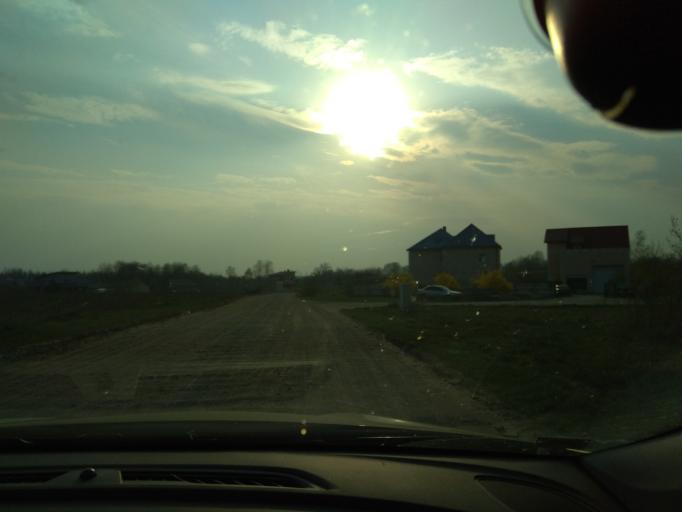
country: LT
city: Baltoji Voke
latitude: 54.5950
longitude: 25.1624
